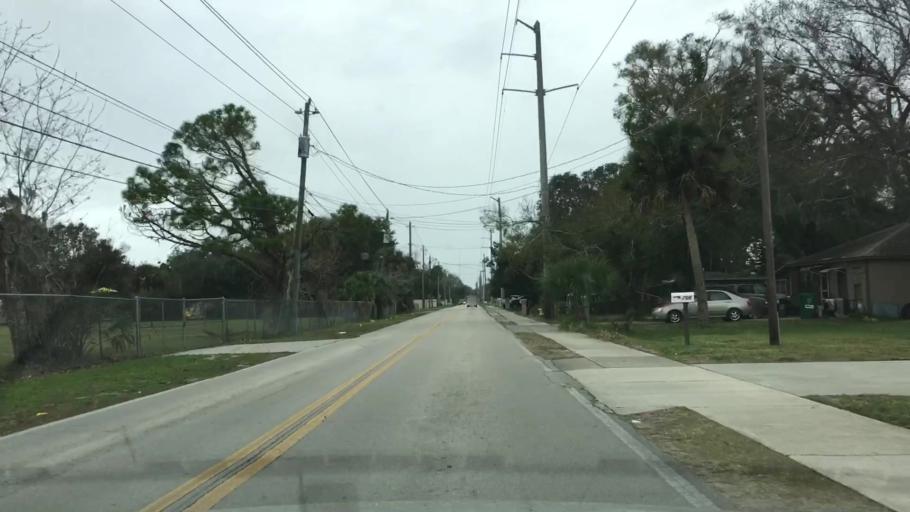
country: US
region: Florida
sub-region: Volusia County
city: Holly Hill
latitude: 29.2447
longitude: -81.0540
